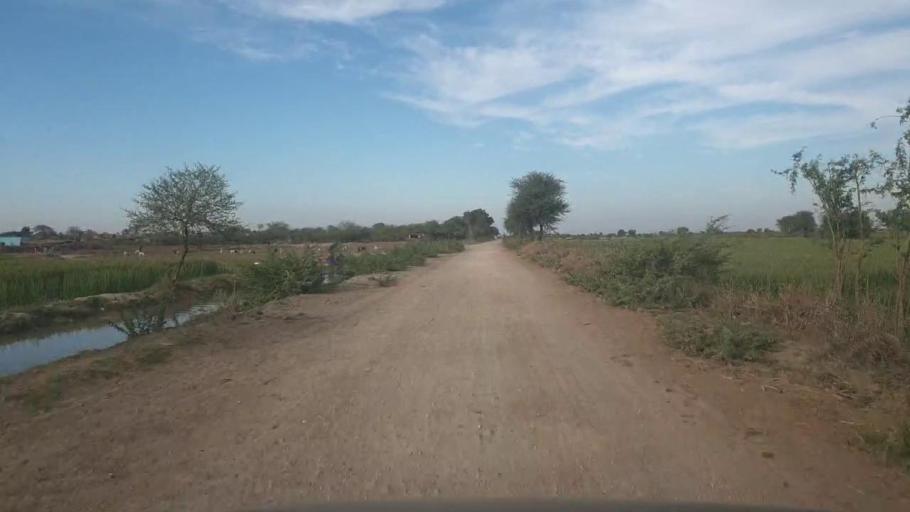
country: PK
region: Sindh
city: Samaro
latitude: 25.3281
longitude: 69.2543
